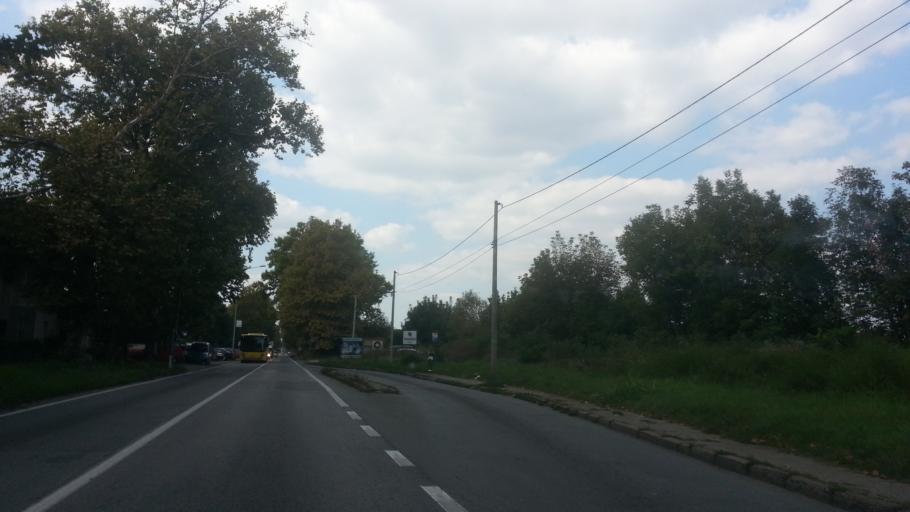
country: RS
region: Central Serbia
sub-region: Belgrade
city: Zemun
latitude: 44.8649
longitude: 20.3645
